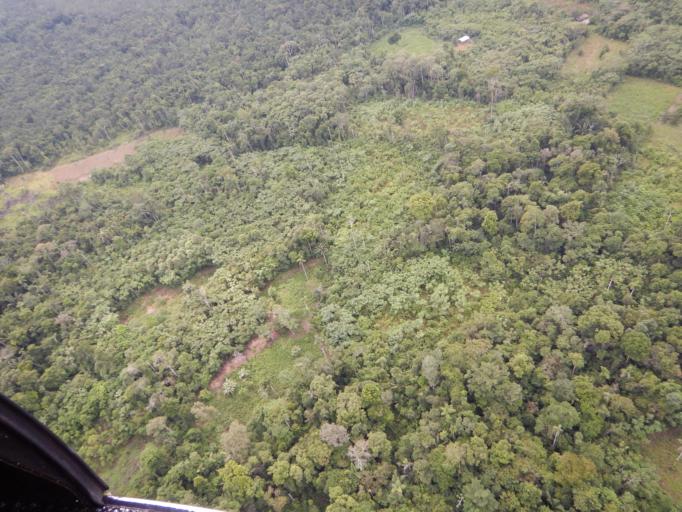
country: BO
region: Cochabamba
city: Chimore
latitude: -16.9208
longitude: -64.9348
